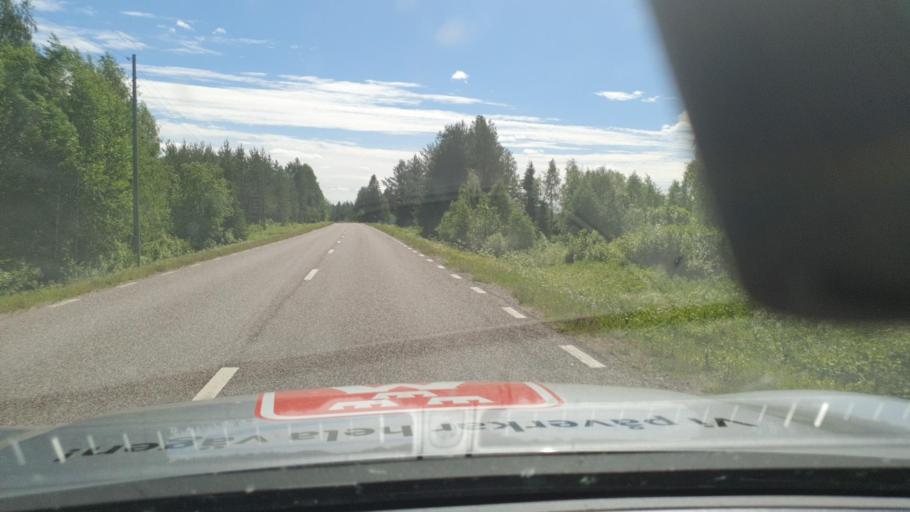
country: FI
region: Lapland
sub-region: Torniolaakso
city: Pello
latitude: 66.9313
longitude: 23.8505
